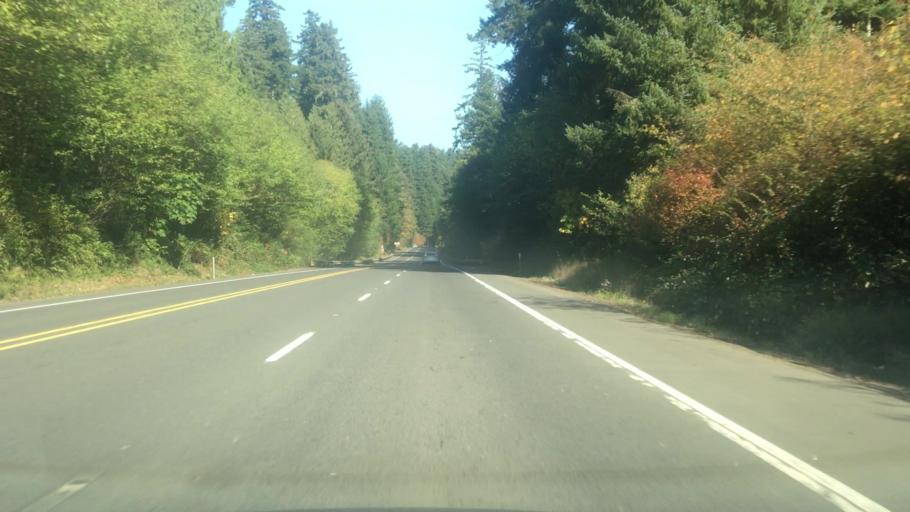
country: US
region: Oregon
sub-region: Lincoln County
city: Rose Lodge
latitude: 45.0425
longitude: -123.8044
